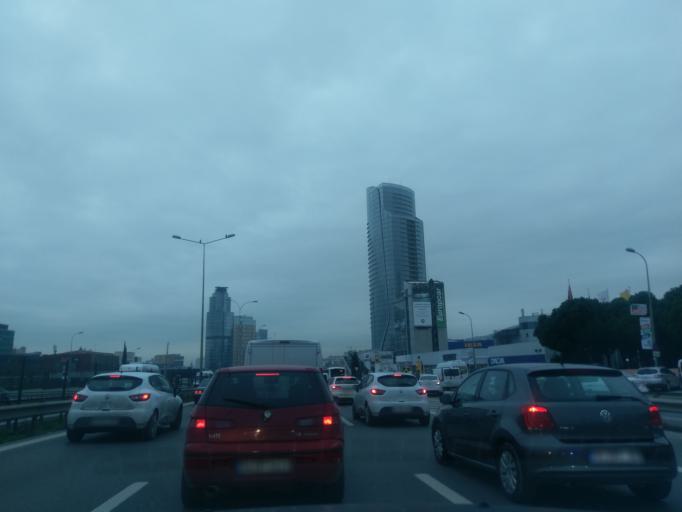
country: TR
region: Istanbul
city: Maltepe
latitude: 40.9165
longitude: 29.1796
